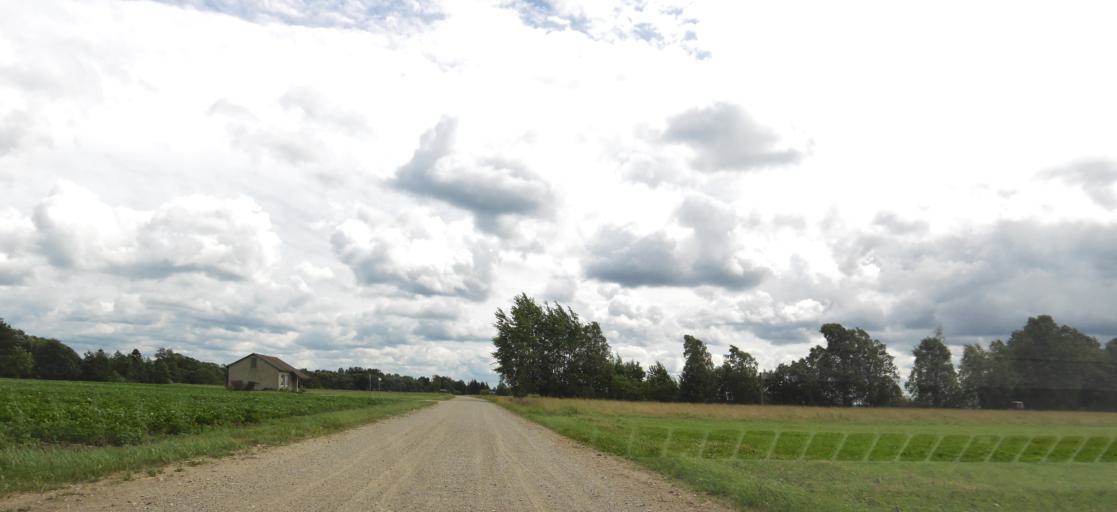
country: LT
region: Panevezys
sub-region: Birzai
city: Birzai
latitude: 56.3166
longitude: 24.8000
